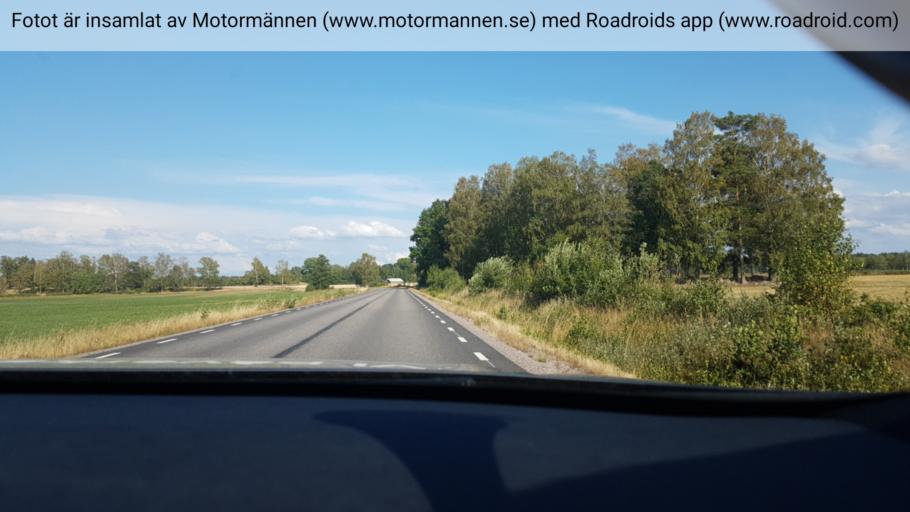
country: SE
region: Vaestra Goetaland
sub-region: Mariestads Kommun
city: Mariestad
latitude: 58.6369
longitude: 13.6600
